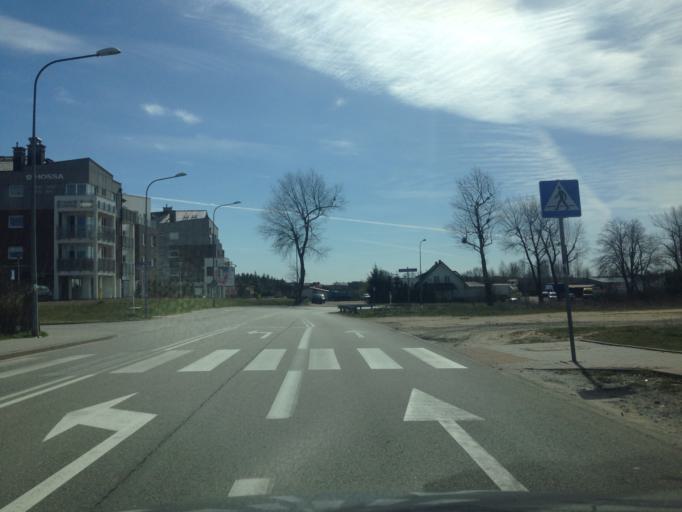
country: PL
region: Pomeranian Voivodeship
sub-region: Powiat wejherowski
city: Bojano
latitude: 54.4945
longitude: 18.4300
